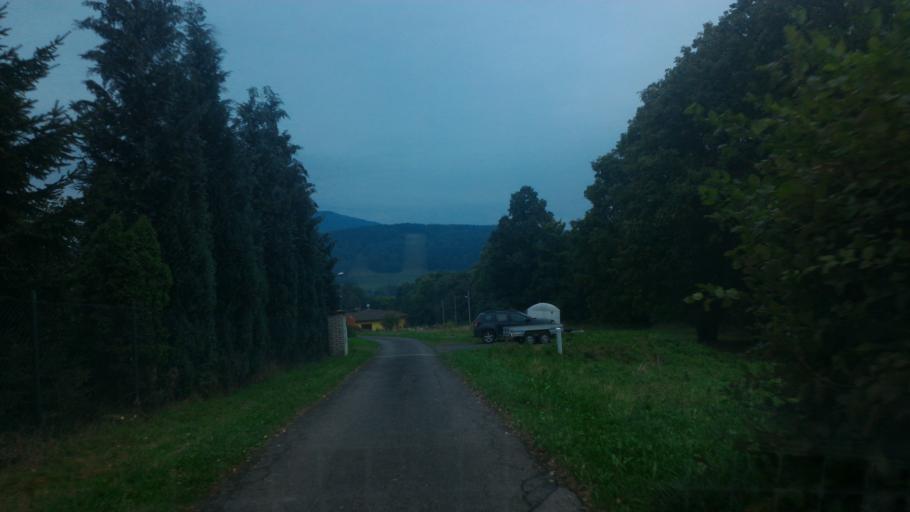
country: CZ
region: Ustecky
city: Dolni Podluzi
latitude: 50.8892
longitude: 14.5578
